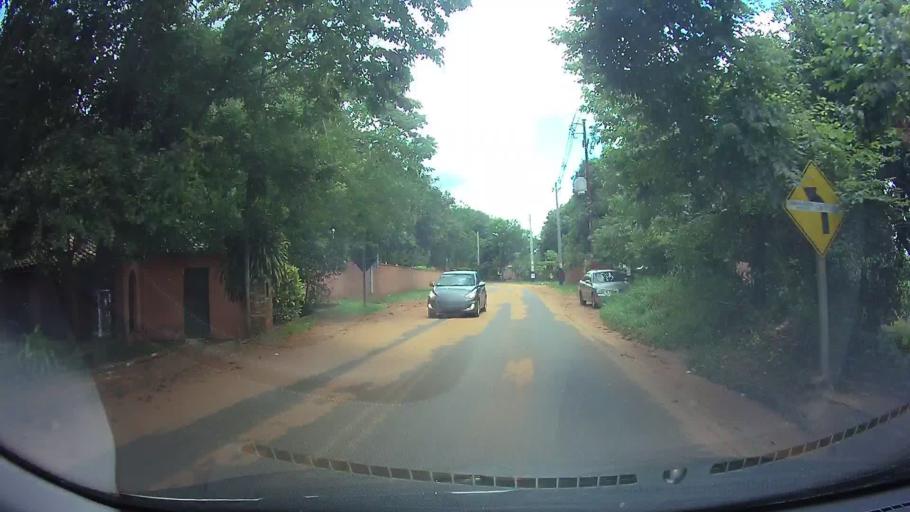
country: PY
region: Central
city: Capiata
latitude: -25.3304
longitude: -57.4222
